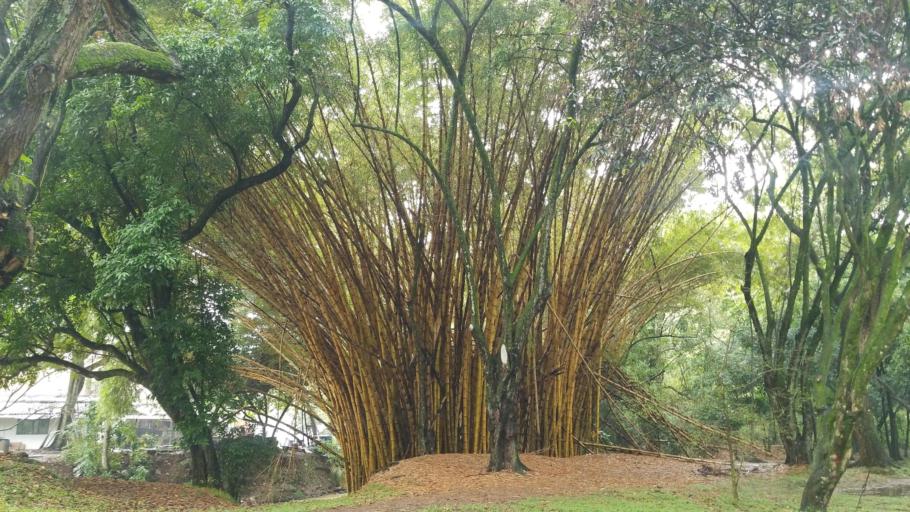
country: CO
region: Valle del Cauca
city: Cali
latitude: 3.3765
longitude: -76.5407
